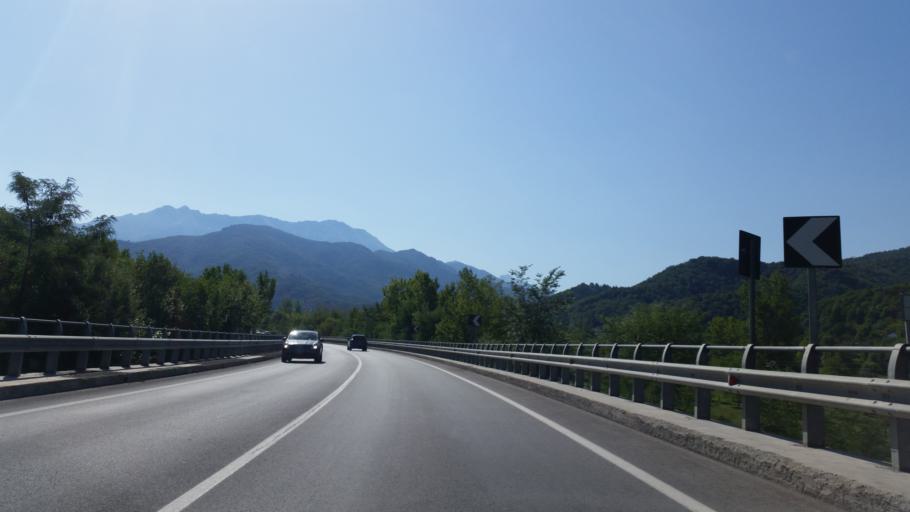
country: IT
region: Piedmont
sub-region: Provincia di Cuneo
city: Roccavione
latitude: 44.3141
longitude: 7.4890
